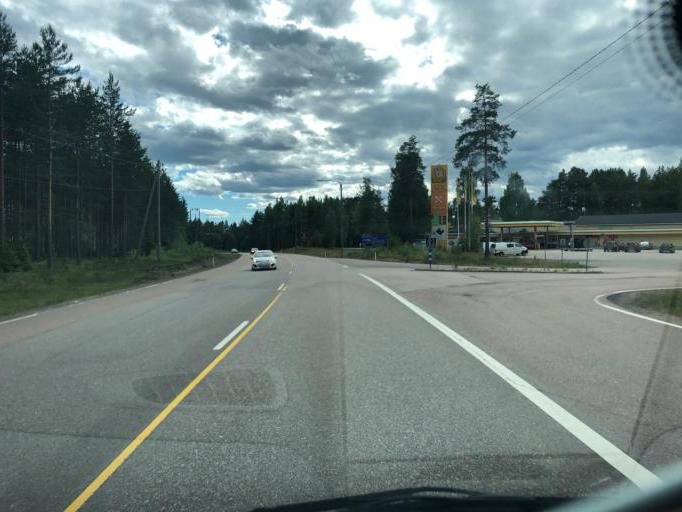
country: FI
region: Southern Savonia
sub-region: Mikkeli
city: Maentyharju
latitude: 61.0921
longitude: 27.0702
